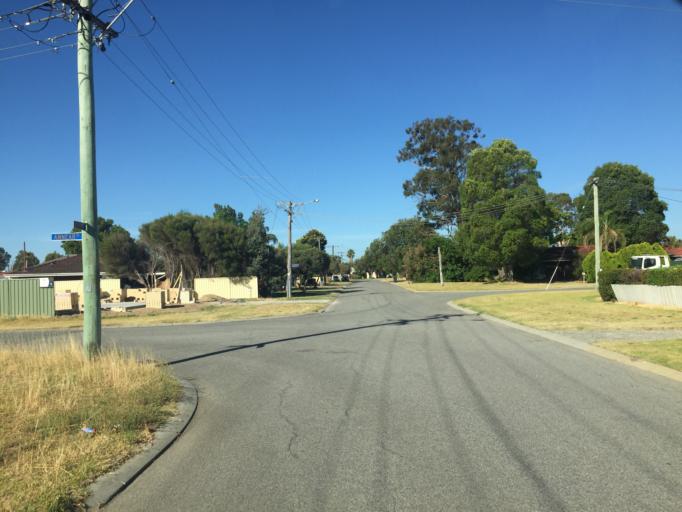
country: AU
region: Western Australia
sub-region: Canning
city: East Cannington
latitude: -32.0133
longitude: 115.9670
